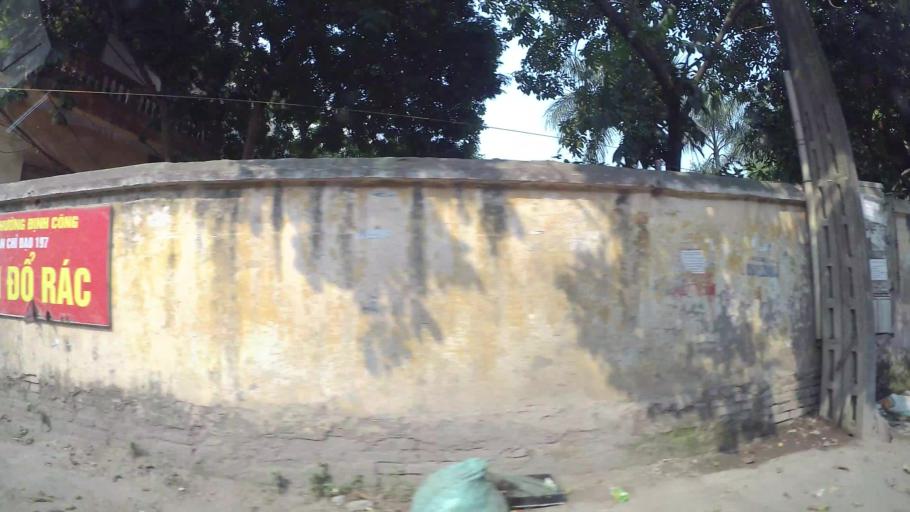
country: VN
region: Ha Noi
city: Thanh Xuan
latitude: 20.9843
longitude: 105.8199
